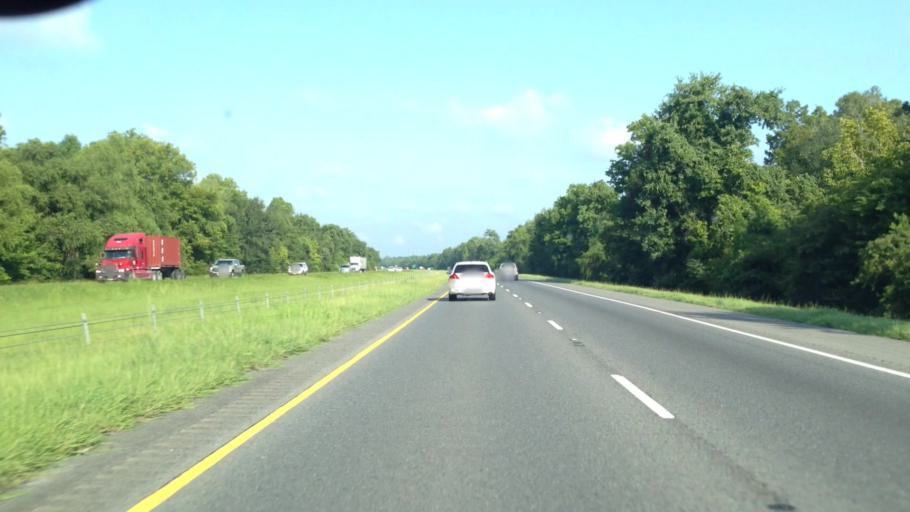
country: US
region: Louisiana
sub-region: Saint James Parish
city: Grand Point
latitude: 30.1475
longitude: -90.7718
